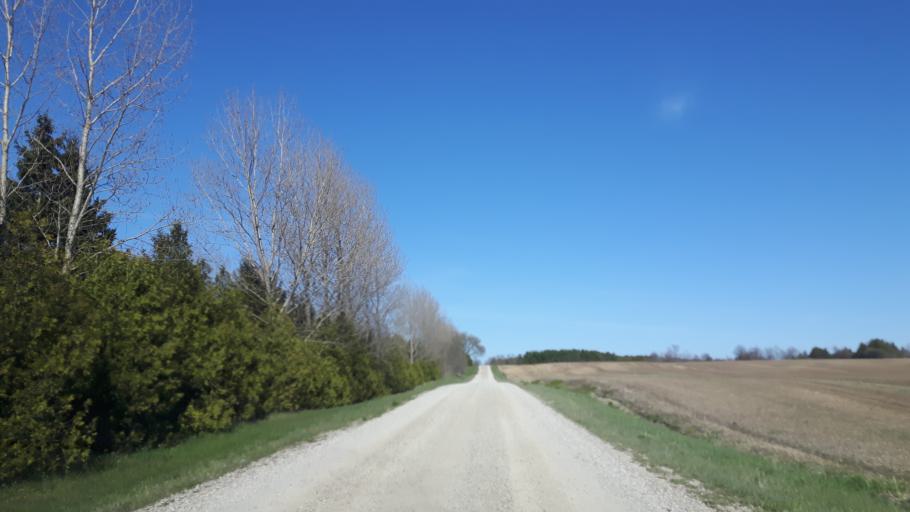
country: CA
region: Ontario
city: Goderich
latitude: 43.6614
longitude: -81.6721
